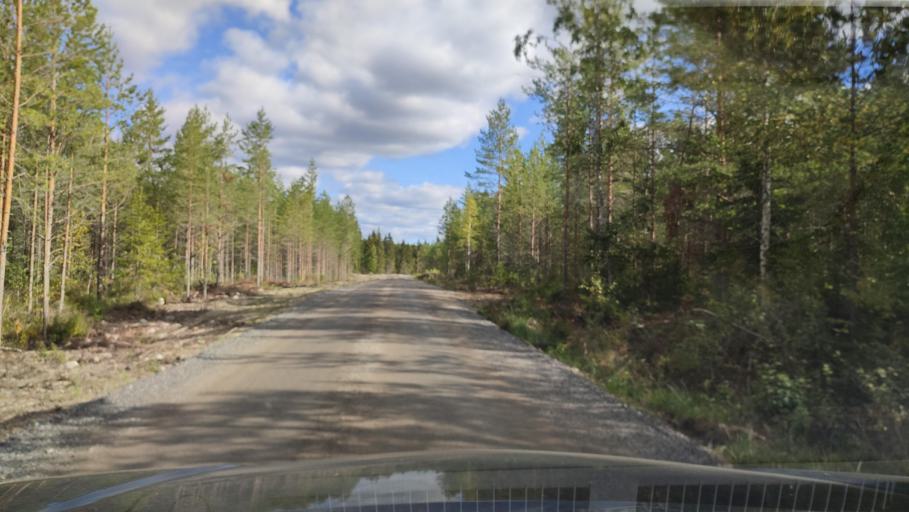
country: FI
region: Southern Ostrobothnia
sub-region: Suupohja
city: Karijoki
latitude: 62.2038
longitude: 21.5896
